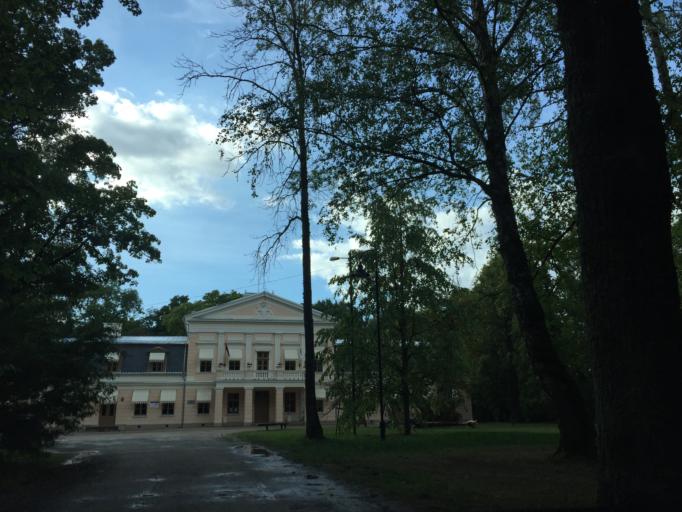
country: LT
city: Zagare
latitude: 56.3618
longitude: 23.2652
